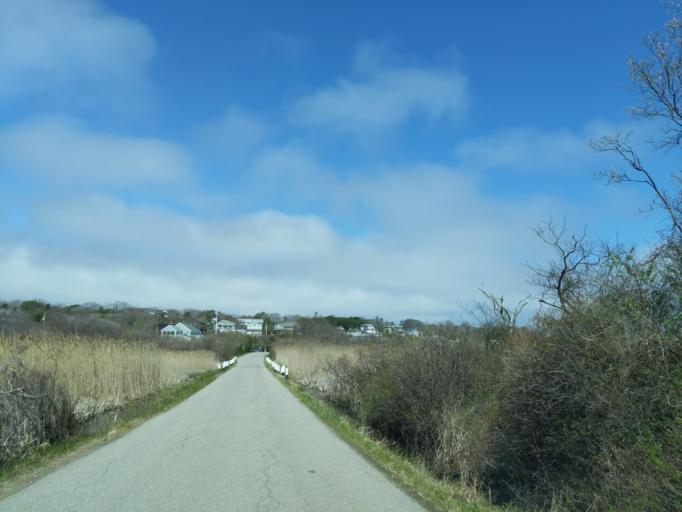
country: US
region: Massachusetts
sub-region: Essex County
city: Rockport
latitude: 42.6390
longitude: -70.5941
